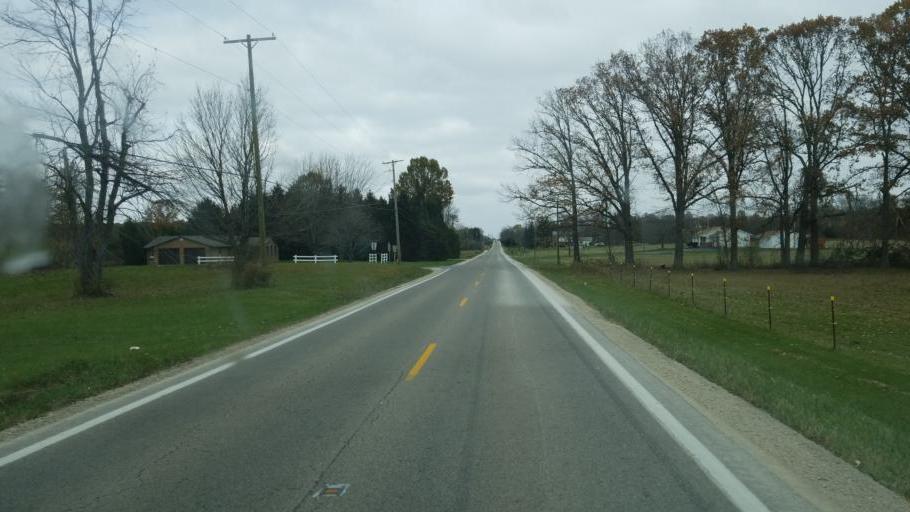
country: US
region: Ohio
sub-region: Crawford County
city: Galion
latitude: 40.6966
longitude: -82.7652
